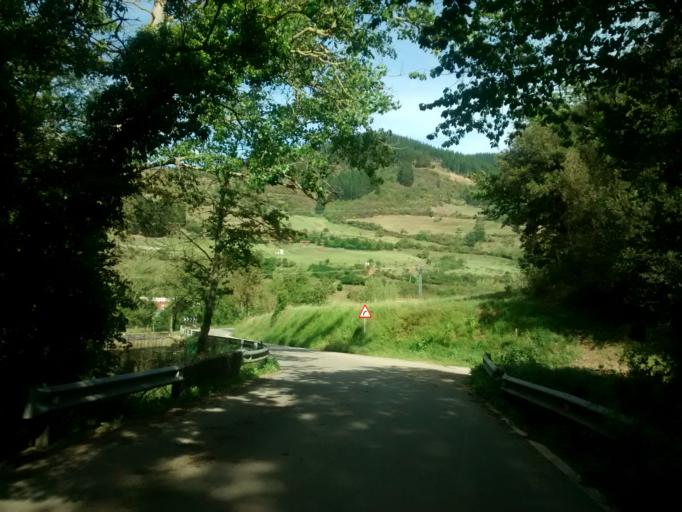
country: ES
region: Cantabria
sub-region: Provincia de Cantabria
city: Potes
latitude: 43.1813
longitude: -4.6059
